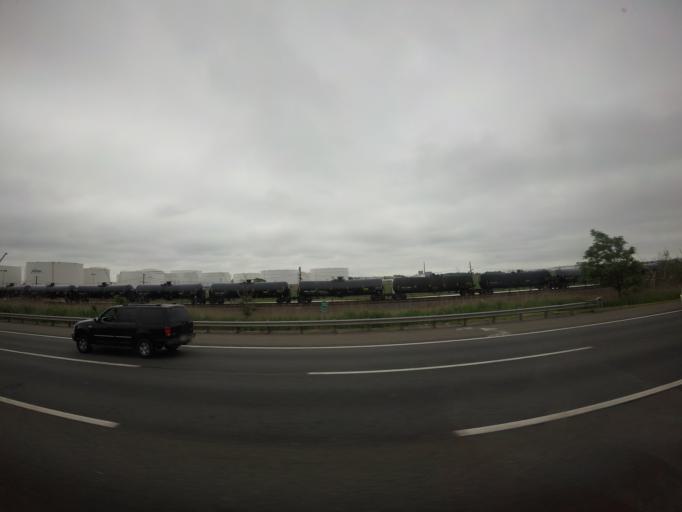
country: US
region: New Jersey
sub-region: Union County
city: Linden
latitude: 40.6085
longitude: -74.2256
